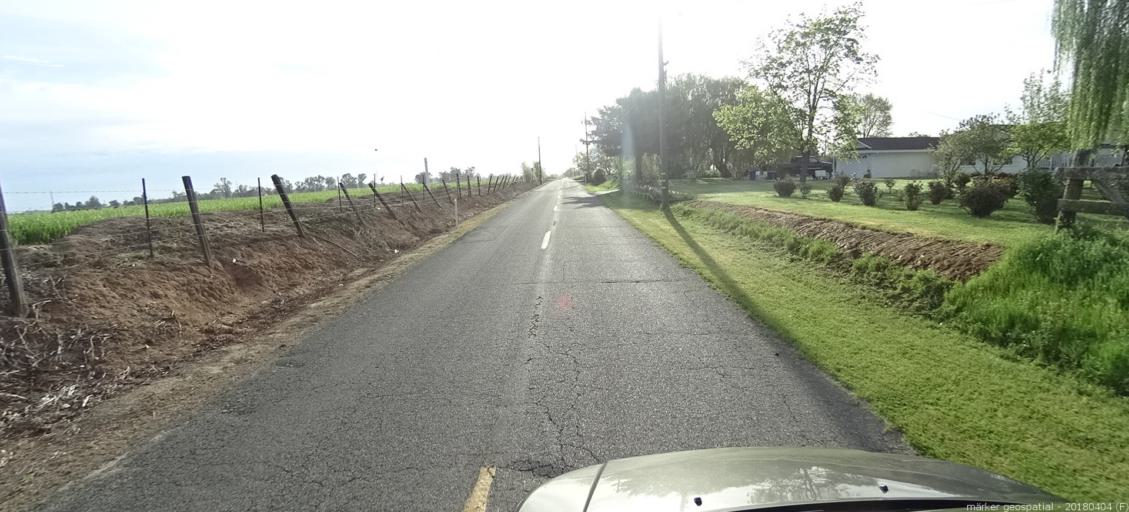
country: US
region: California
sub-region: Sacramento County
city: Herald
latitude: 38.3361
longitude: -121.2625
